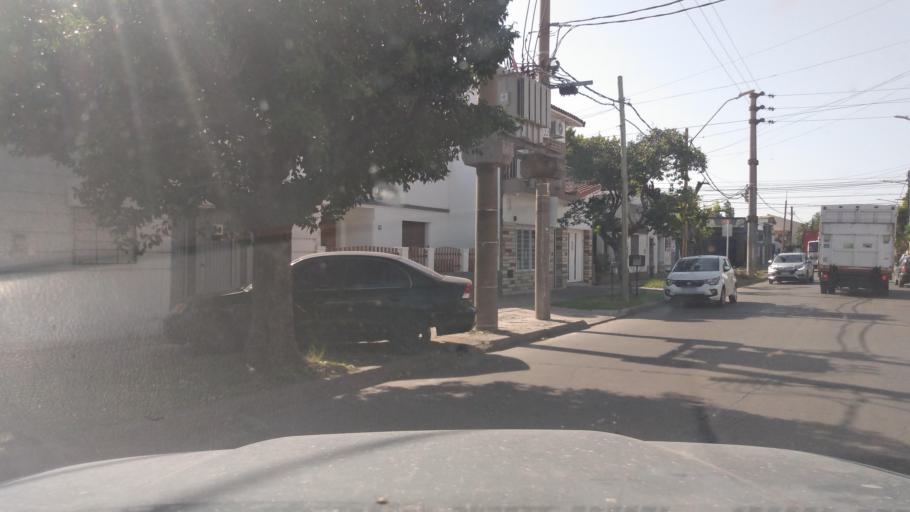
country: AR
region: Buenos Aires
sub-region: Partido de Moron
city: Moron
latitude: -34.6508
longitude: -58.5951
